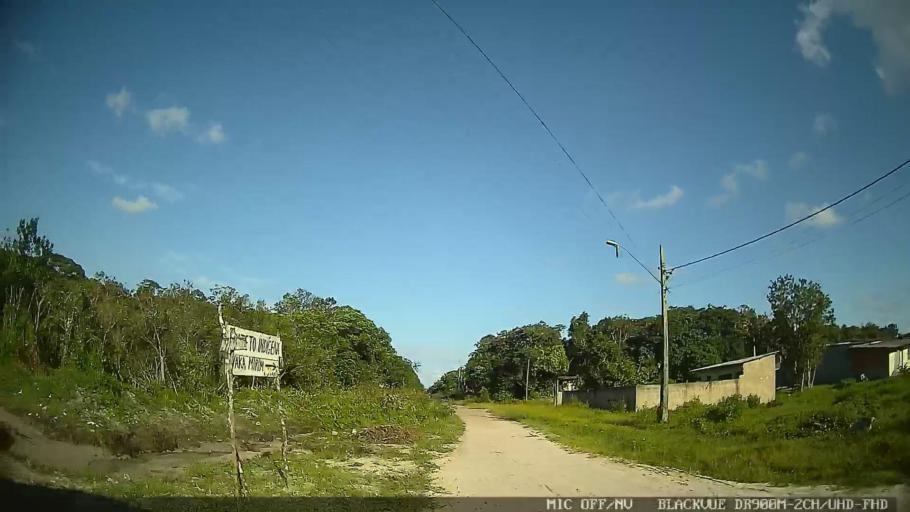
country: BR
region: Sao Paulo
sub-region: Itanhaem
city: Itanhaem
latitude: -24.1588
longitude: -46.8297
